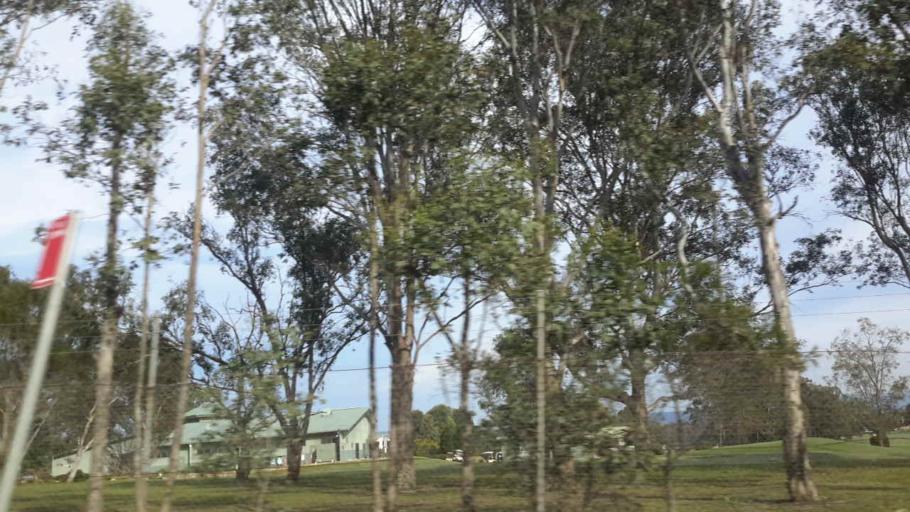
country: AU
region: New South Wales
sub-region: Penrith Municipality
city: Kingswood Park
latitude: -33.7908
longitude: 150.6998
